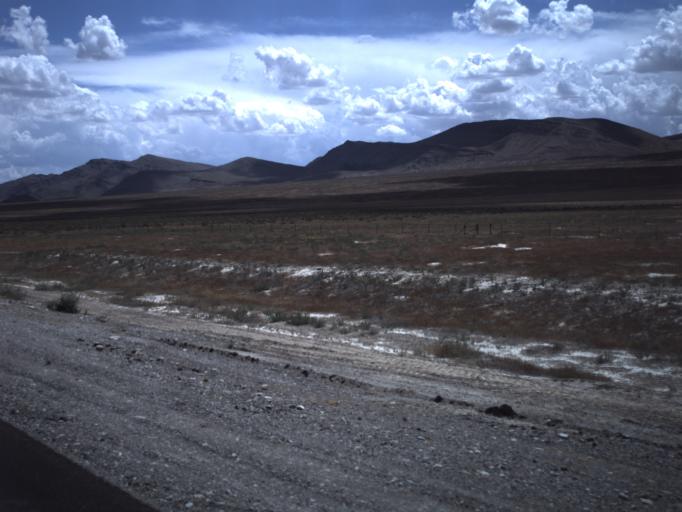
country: US
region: Utah
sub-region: Beaver County
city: Milford
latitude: 39.0824
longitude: -113.4929
